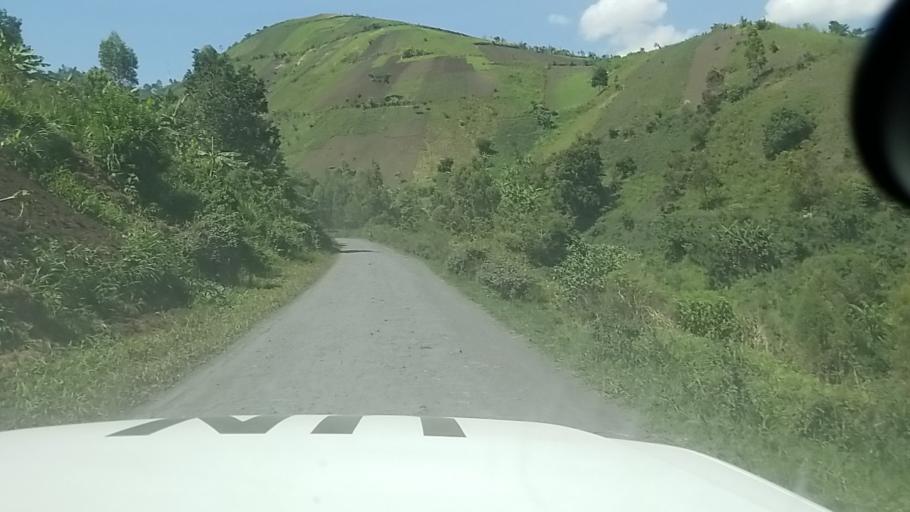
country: CD
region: Nord Kivu
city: Sake
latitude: -1.7425
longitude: 28.9938
